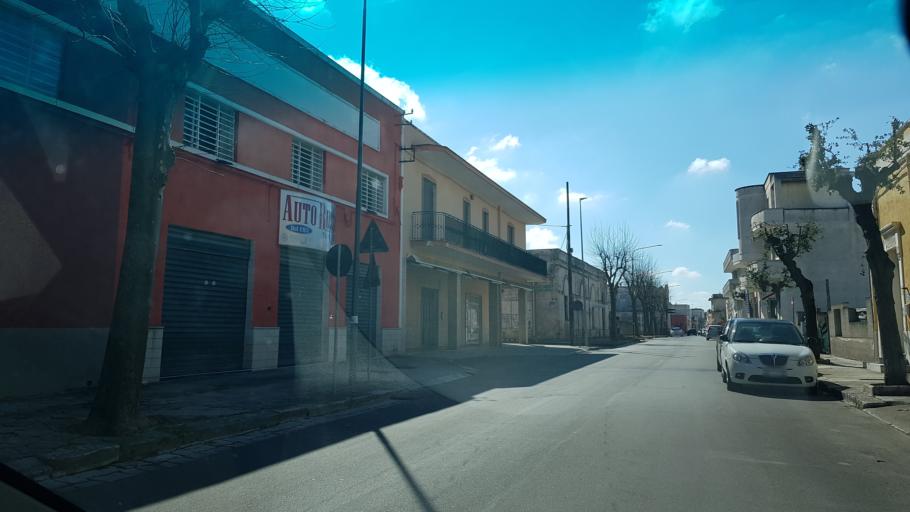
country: IT
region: Apulia
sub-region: Provincia di Lecce
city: Salice Salentino
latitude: 40.3881
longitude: 17.9669
